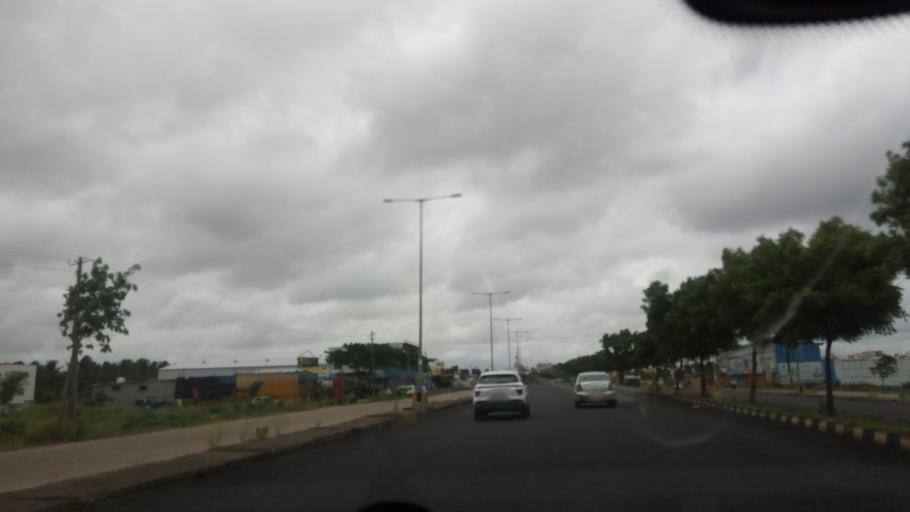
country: IN
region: Karnataka
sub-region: Mysore
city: Mysore
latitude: 12.3252
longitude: 76.5963
